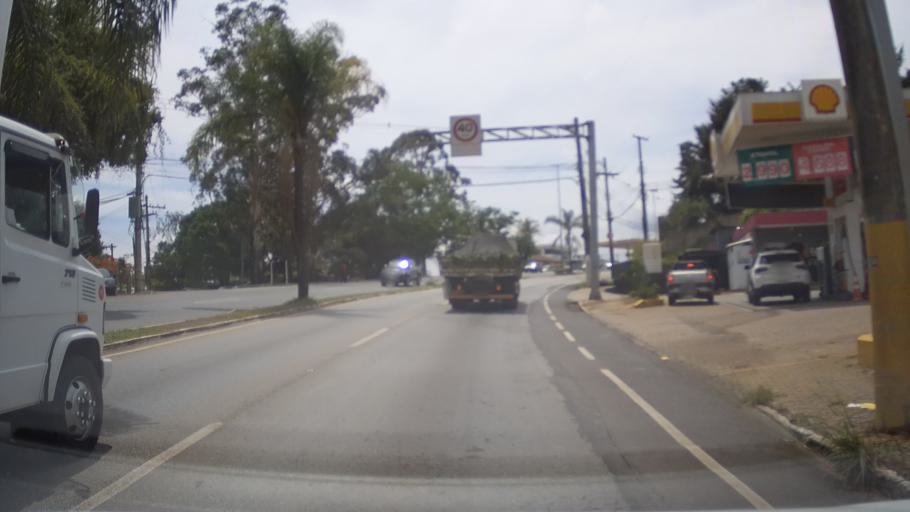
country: BR
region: Minas Gerais
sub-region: Nova Lima
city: Nova Lima
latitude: -19.9989
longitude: -43.8936
